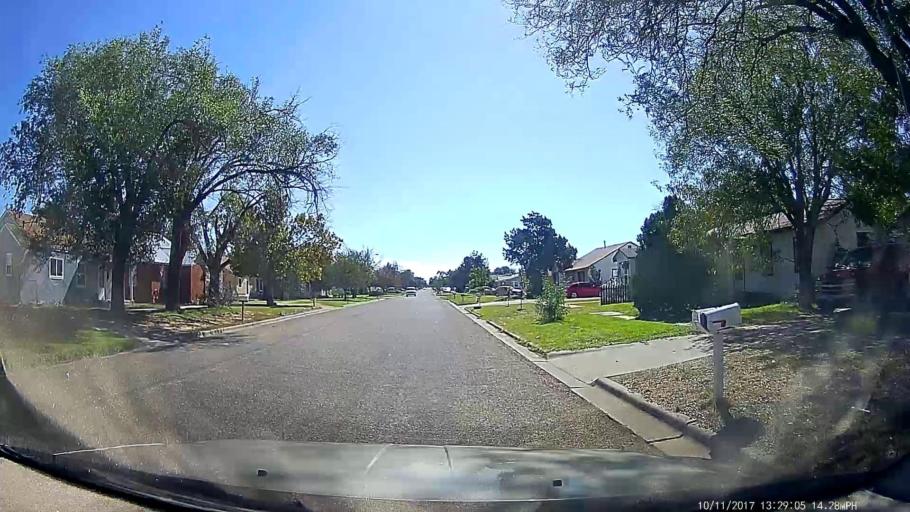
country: US
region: New Mexico
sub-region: Curry County
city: Clovis
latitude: 34.4095
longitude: -103.2118
